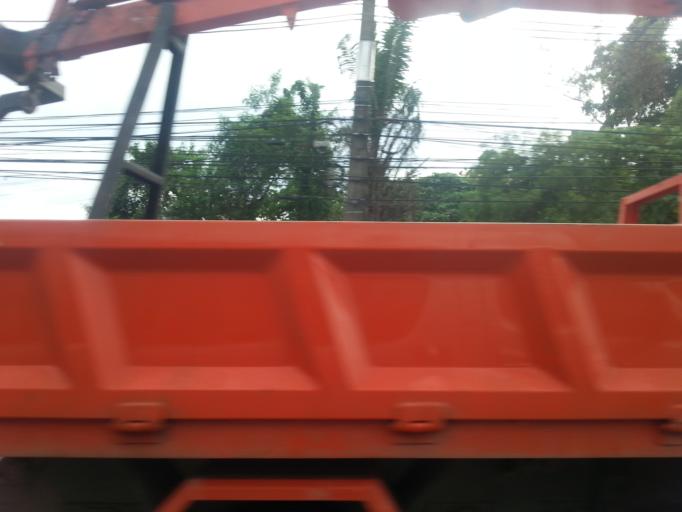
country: TH
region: Krabi
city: Krabi
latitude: 8.1025
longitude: 98.9052
